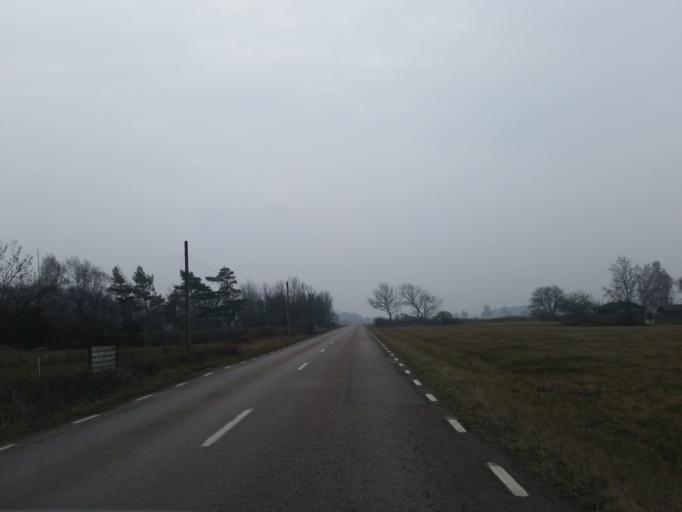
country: SE
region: Kalmar
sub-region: Morbylanga Kommun
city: Moerbylanga
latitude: 56.4170
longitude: 16.4136
